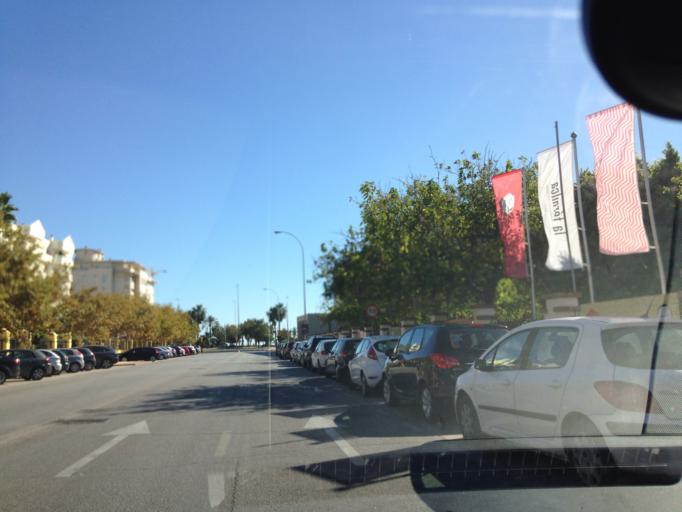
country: ES
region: Andalusia
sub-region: Provincia de Malaga
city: Malaga
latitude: 36.6901
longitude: -4.4450
